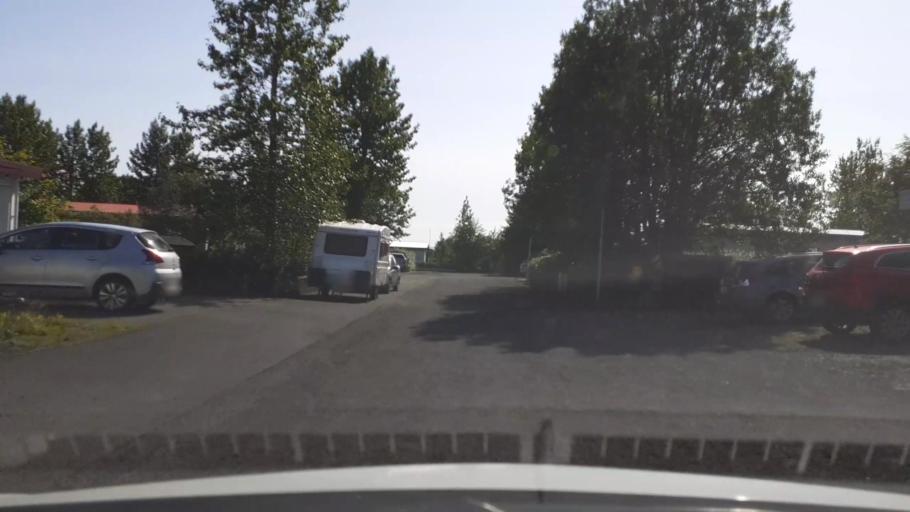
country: IS
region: South
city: Hveragerdi
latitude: 64.0046
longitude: -21.2025
